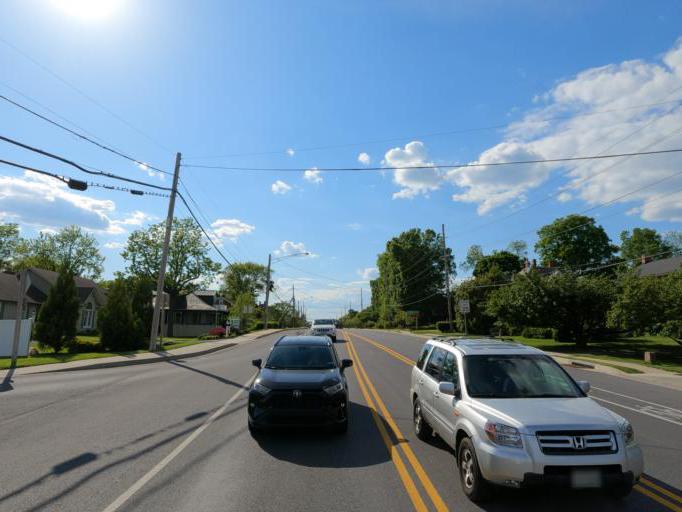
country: US
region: Maryland
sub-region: Frederick County
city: Middletown
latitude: 39.4380
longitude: -77.5278
